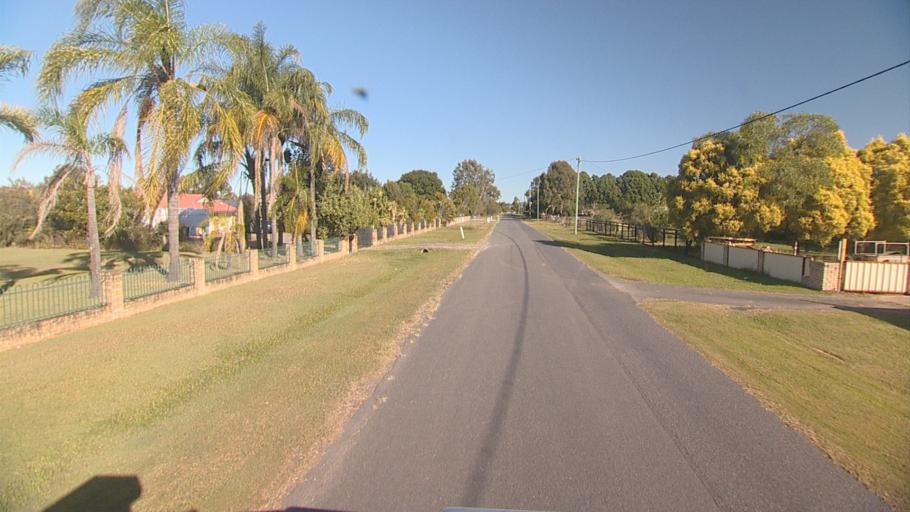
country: AU
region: Queensland
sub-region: Logan
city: Logan Reserve
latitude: -27.7391
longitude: 153.1134
